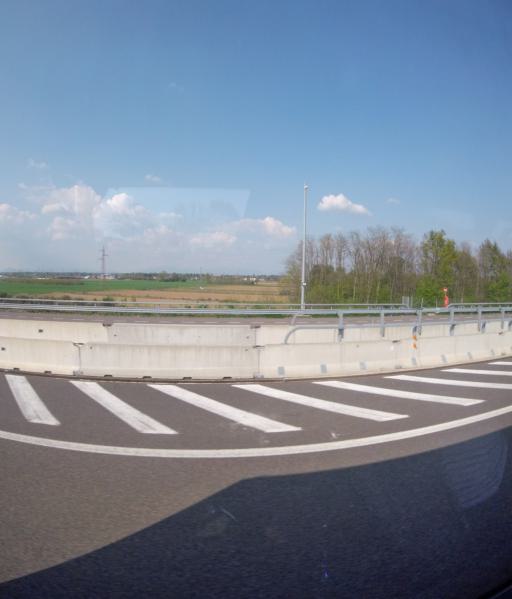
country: IT
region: Lombardy
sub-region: Provincia di Como
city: Mozzate
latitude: 45.6613
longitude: 8.9476
